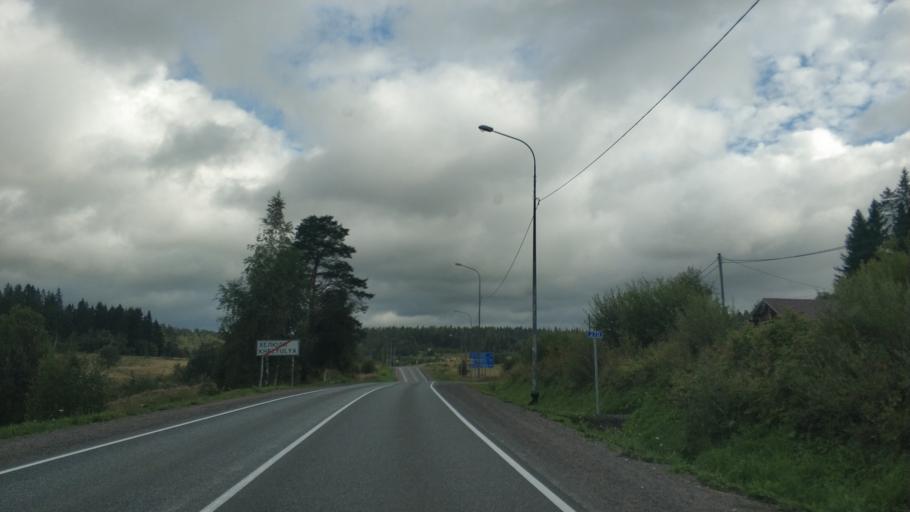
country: RU
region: Republic of Karelia
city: Khelyulya
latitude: 61.7564
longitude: 30.6567
